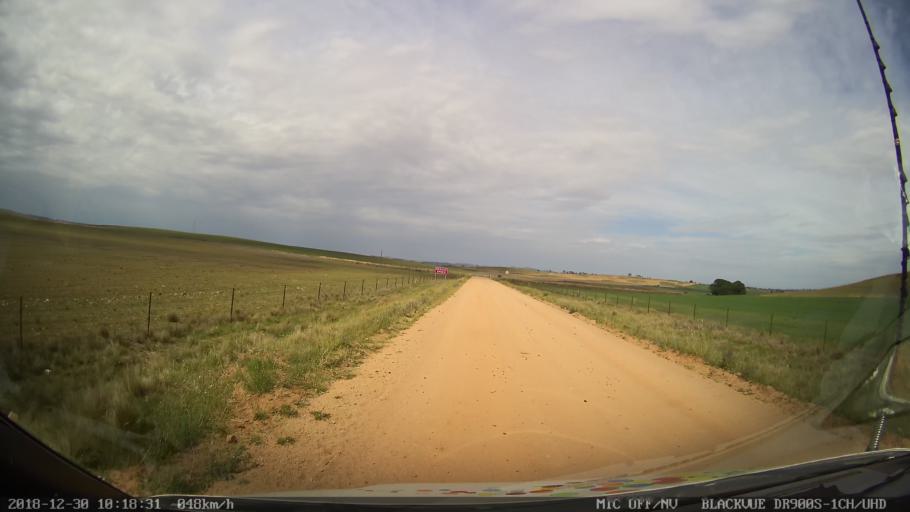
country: AU
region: New South Wales
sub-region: Snowy River
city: Berridale
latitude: -36.5523
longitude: 149.0087
